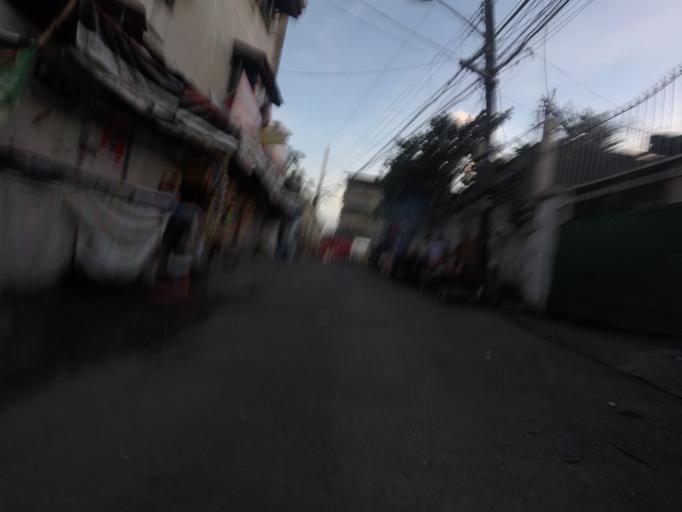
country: PH
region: Metro Manila
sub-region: San Juan
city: San Juan
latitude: 14.5970
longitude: 121.0339
